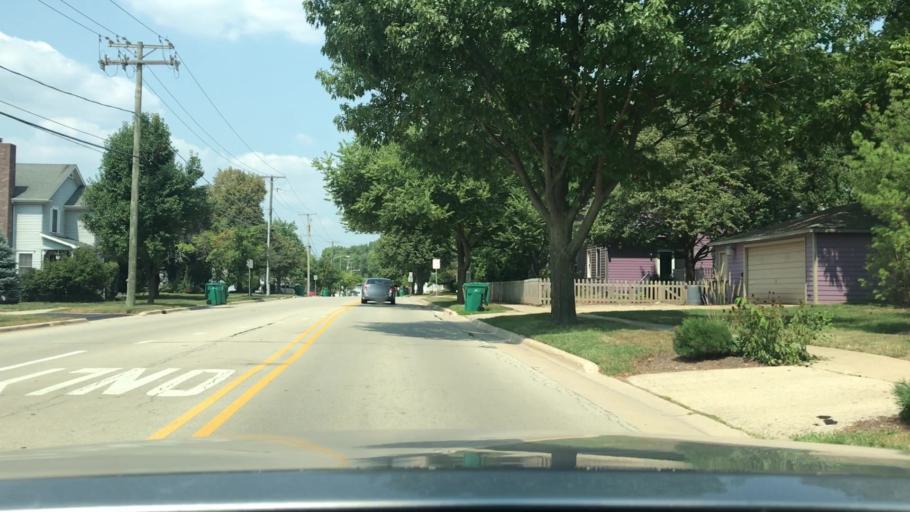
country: US
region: Illinois
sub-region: Will County
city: Plainfield
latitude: 41.6058
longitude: -88.2083
